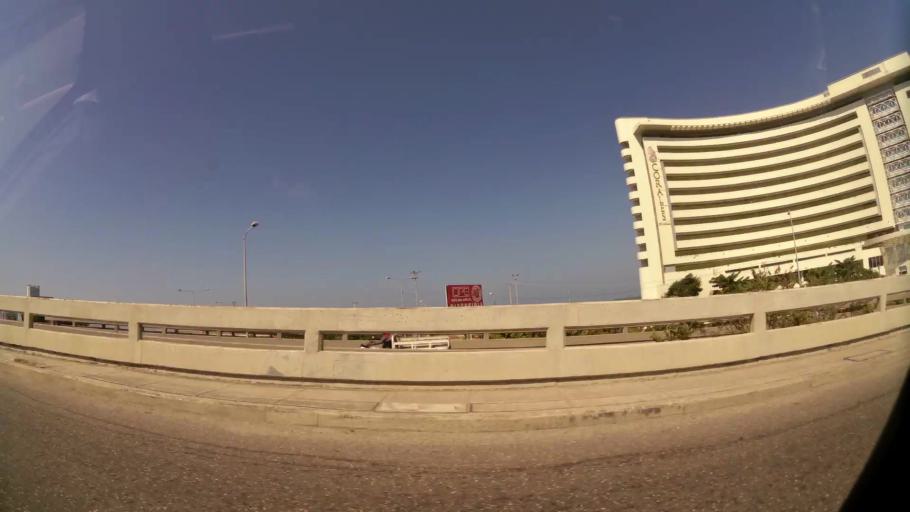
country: CO
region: Bolivar
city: Cartagena
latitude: 10.4424
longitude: -75.5254
